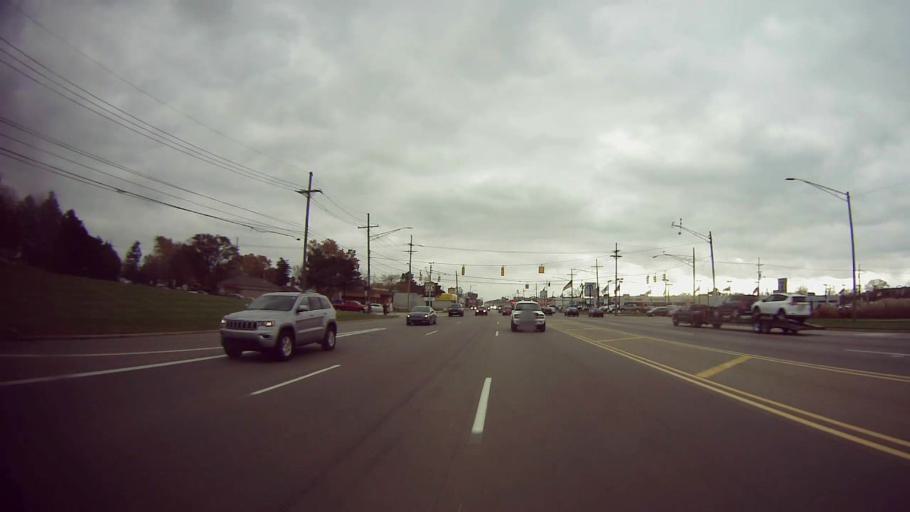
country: US
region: Michigan
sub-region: Macomb County
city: Sterling Heights
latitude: 42.5373
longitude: -83.0292
